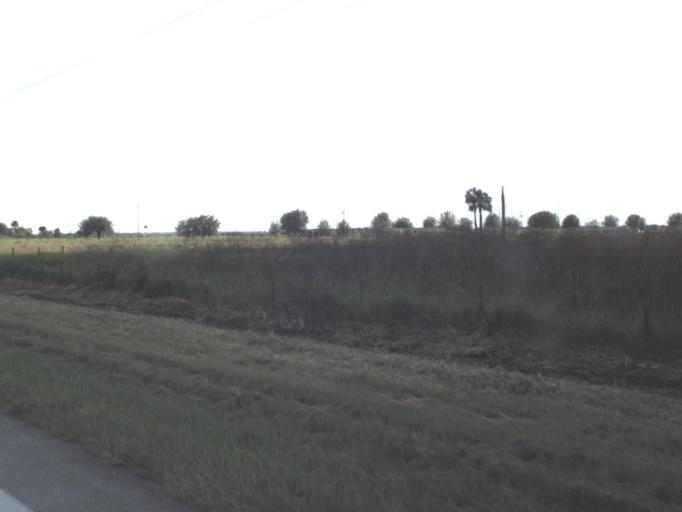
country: US
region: Florida
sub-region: Okeechobee County
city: Okeechobee
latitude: 27.3609
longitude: -80.9654
